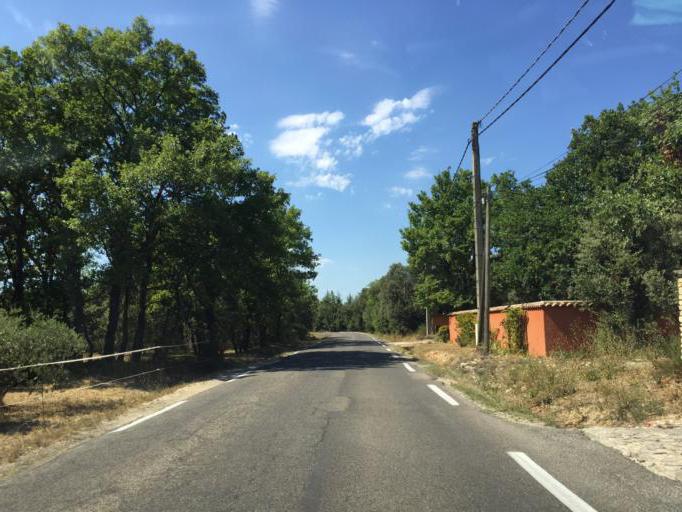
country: FR
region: Provence-Alpes-Cote d'Azur
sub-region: Departement du Vaucluse
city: Malemort-du-Comtat
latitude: 44.0144
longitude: 5.1346
